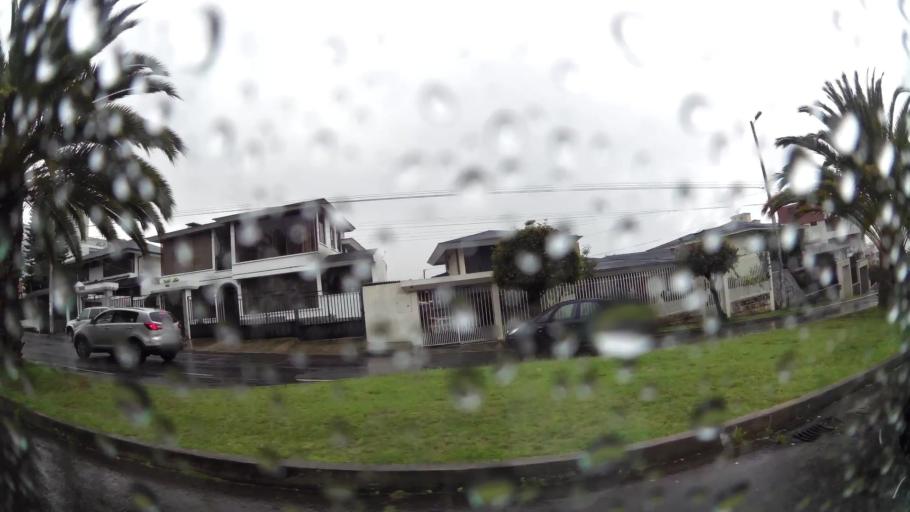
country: EC
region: Pichincha
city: Quito
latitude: -0.1041
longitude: -78.5045
